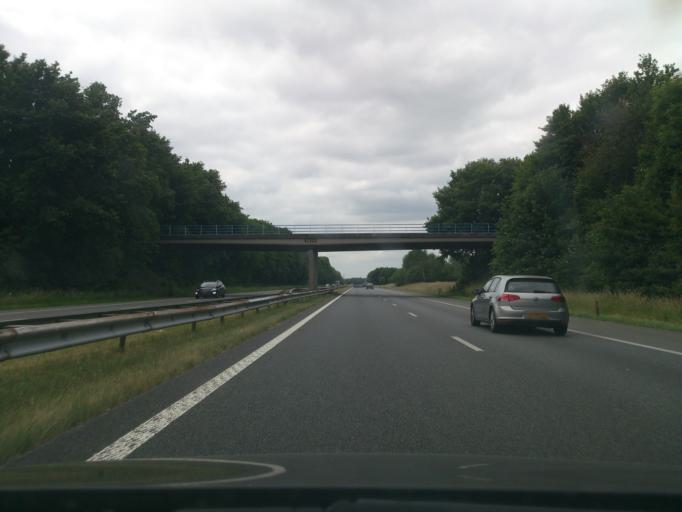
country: NL
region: Gelderland
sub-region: Gemeente Wijchen
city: Wijchen
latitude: 51.8226
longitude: 5.7222
